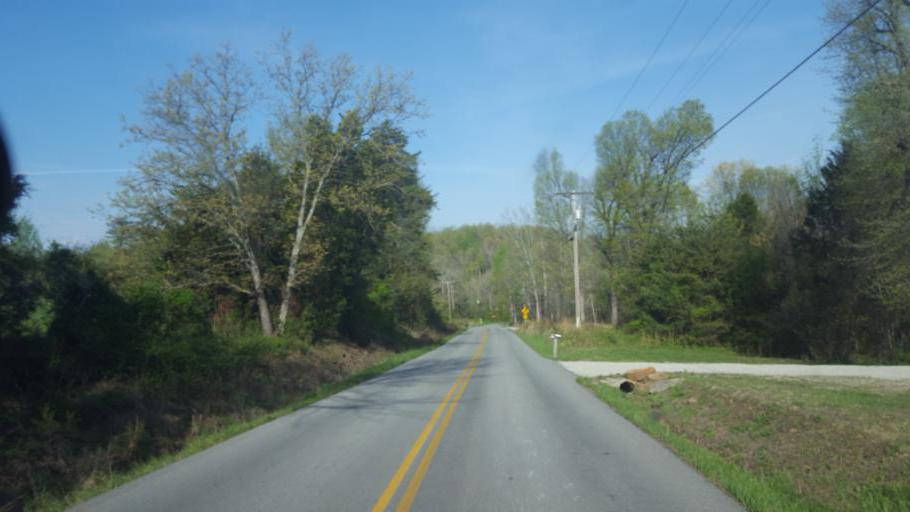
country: US
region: Kentucky
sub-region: Edmonson County
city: Brownsville
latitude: 37.3190
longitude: -86.1121
